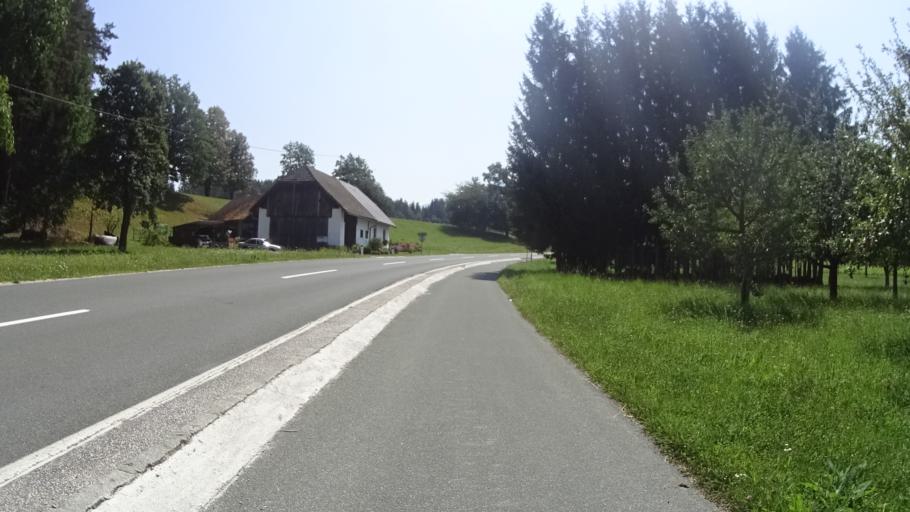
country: AT
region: Carinthia
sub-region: Politischer Bezirk Volkermarkt
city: Eberndorf
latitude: 46.5732
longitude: 14.6600
